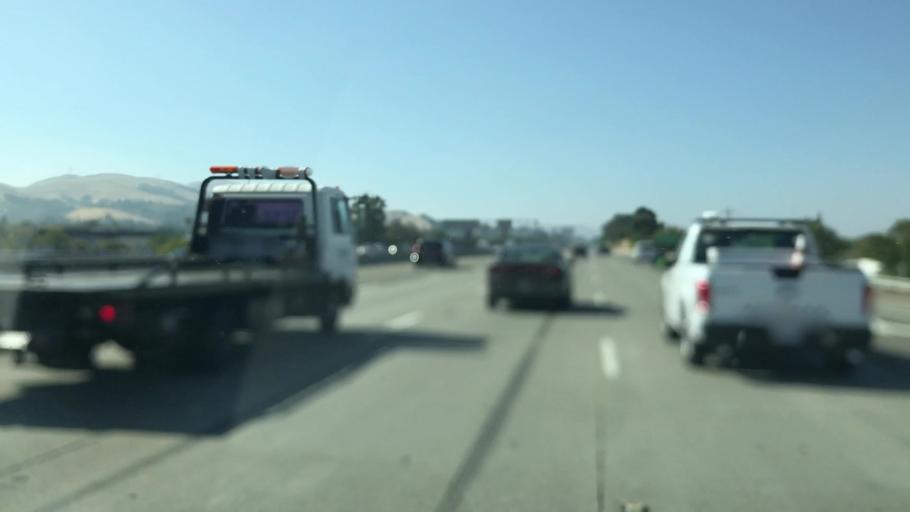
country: US
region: California
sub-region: Alameda County
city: Dublin
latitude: 37.7083
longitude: -121.9274
